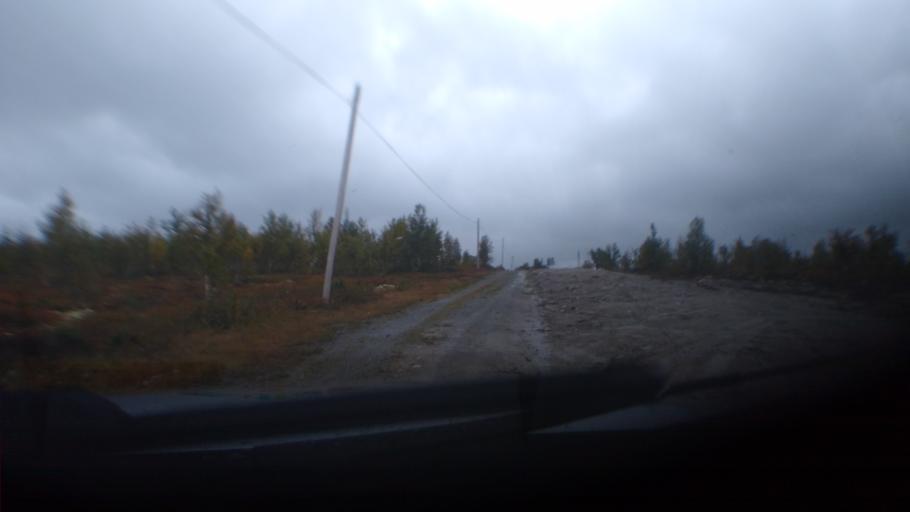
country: NO
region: Oppland
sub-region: Ringebu
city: Ringebu
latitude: 61.6623
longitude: 10.1036
